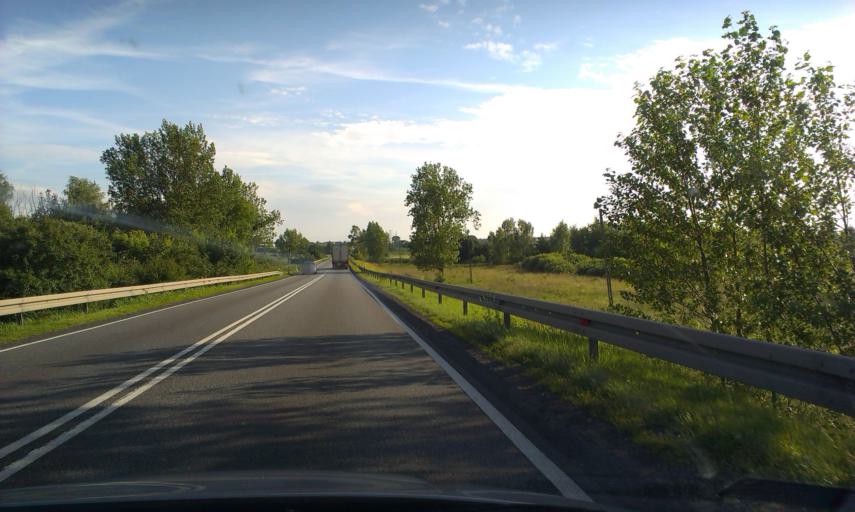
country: PL
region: Kujawsko-Pomorskie
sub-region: Powiat bydgoski
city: Biale Blota
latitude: 53.1450
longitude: 17.8818
